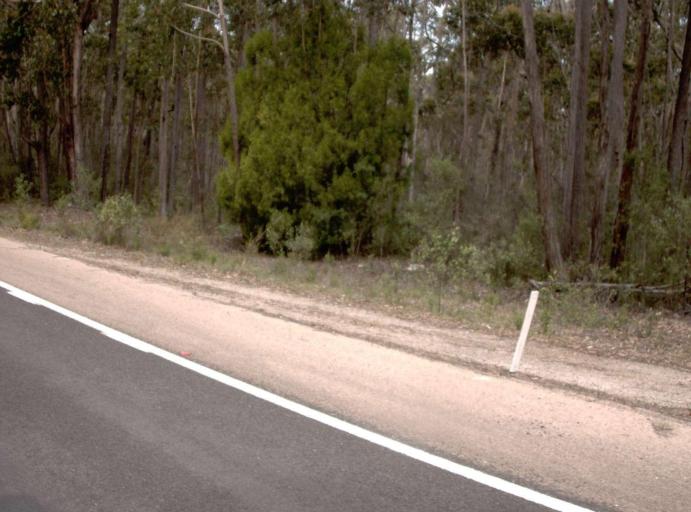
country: AU
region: New South Wales
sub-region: Bega Valley
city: Eden
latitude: -37.5079
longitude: 149.5252
